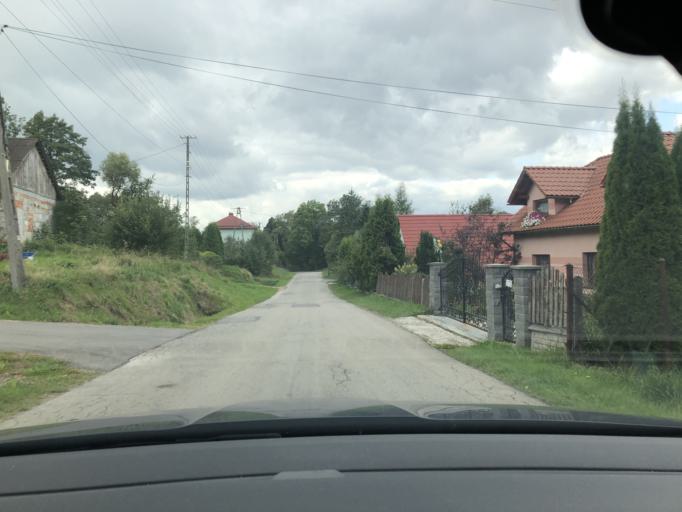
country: PL
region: Silesian Voivodeship
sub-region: Powiat zywiecki
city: Slemien
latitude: 49.7243
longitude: 19.3951
